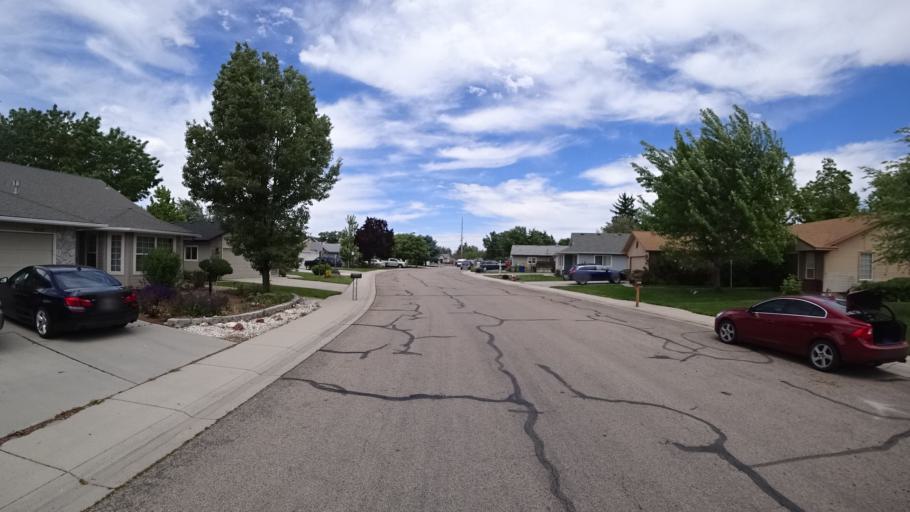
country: US
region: Idaho
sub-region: Ada County
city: Meridian
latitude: 43.6324
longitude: -116.3271
